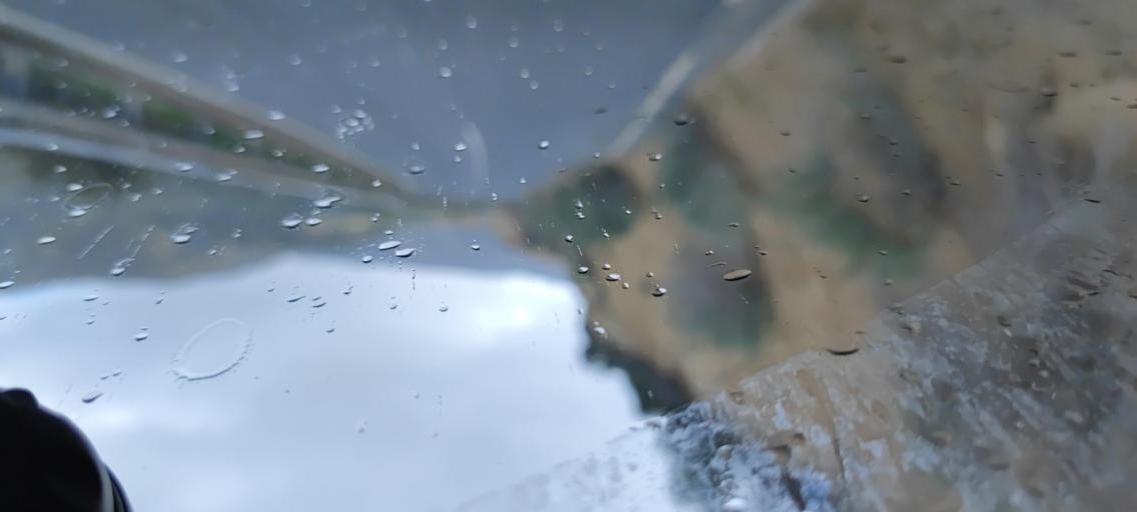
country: CY
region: Limassol
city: Pissouri
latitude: 34.6525
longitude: 32.7226
